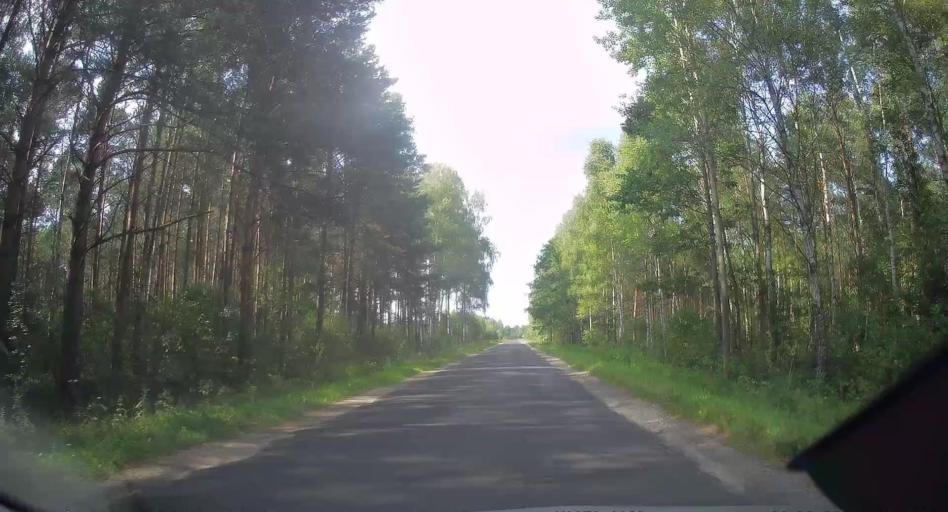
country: PL
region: Swietokrzyskie
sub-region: Powiat konecki
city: Radoszyce
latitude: 51.1059
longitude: 20.2652
